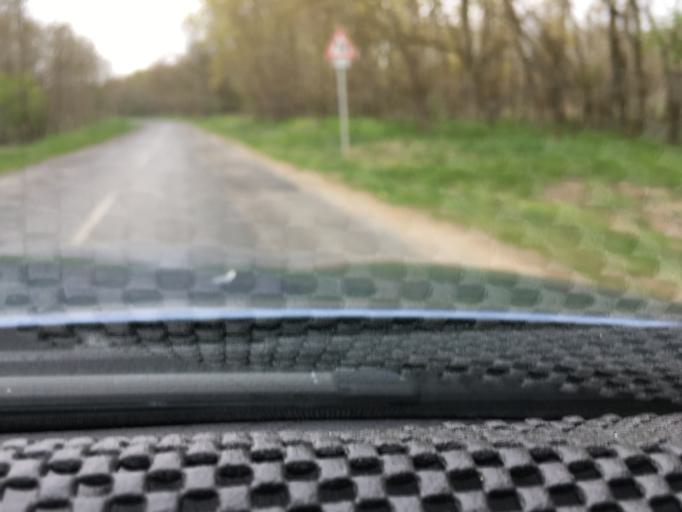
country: HU
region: Hajdu-Bihar
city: Nyiradony
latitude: 47.6910
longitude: 21.9402
